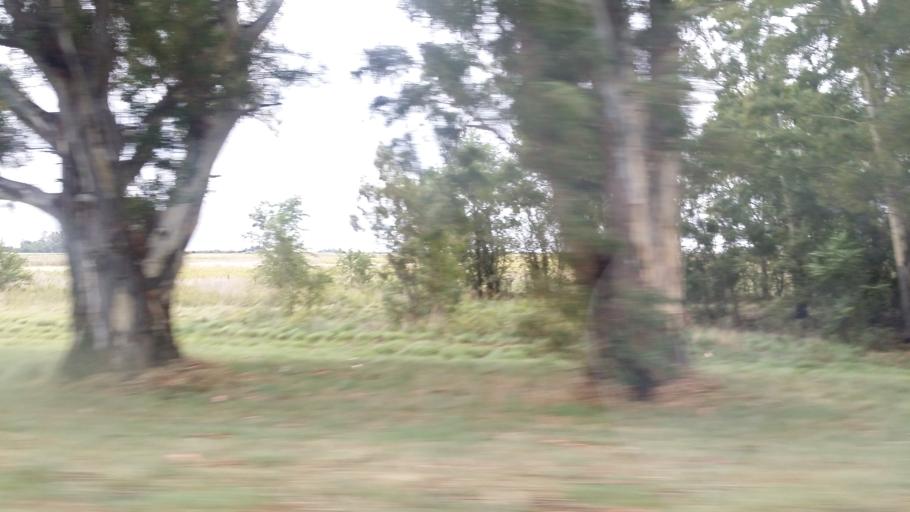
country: AR
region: La Pampa
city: Lonquimay
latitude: -36.4993
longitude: -63.6864
